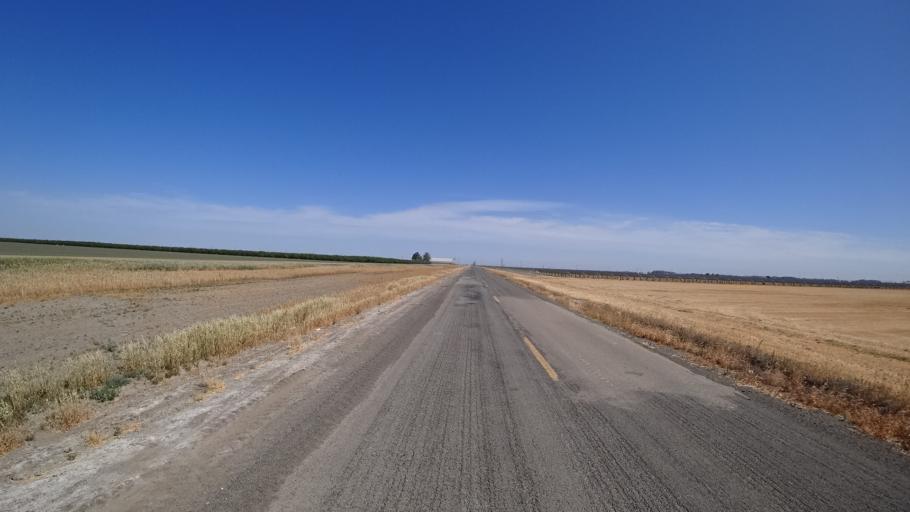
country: US
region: California
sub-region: Kings County
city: Stratford
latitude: 36.2161
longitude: -119.8341
